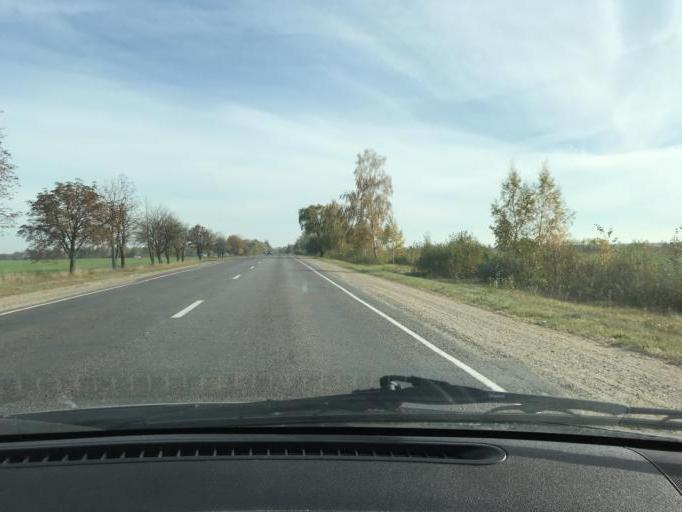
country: BY
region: Brest
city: Asnyezhytsy
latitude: 52.2054
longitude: 26.0557
